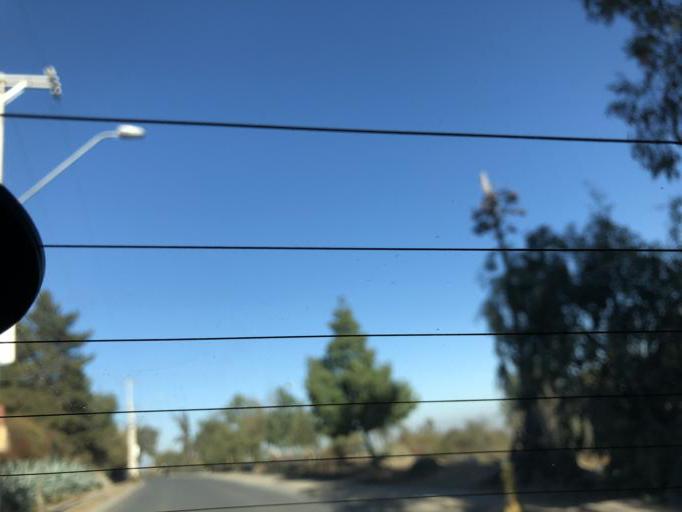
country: CL
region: Santiago Metropolitan
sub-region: Provincia de Cordillera
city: Puente Alto
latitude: -33.5610
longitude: -70.5369
